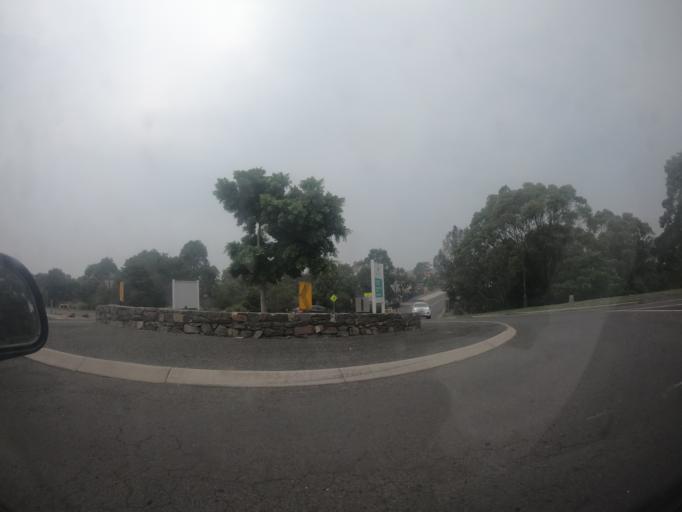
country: AU
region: New South Wales
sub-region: Shellharbour
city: Flinders
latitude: -34.5951
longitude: 150.8535
